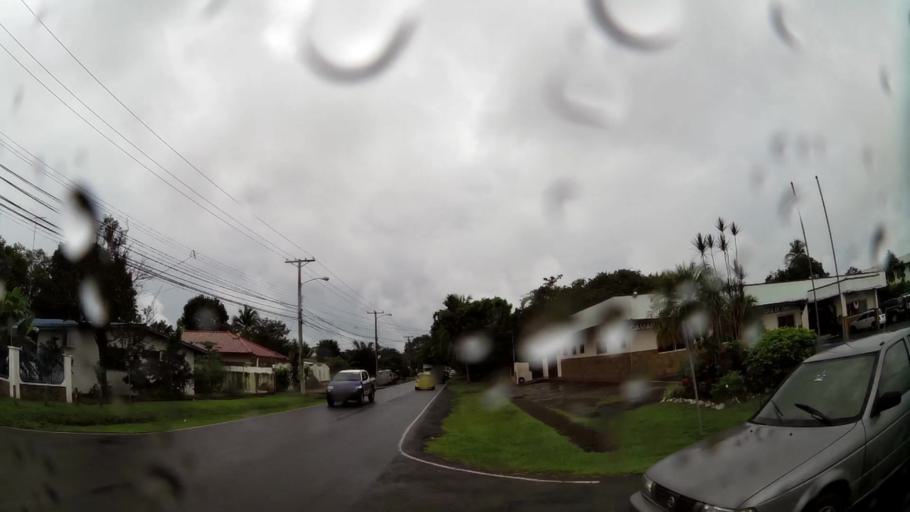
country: PA
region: Chiriqui
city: David
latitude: 8.4320
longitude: -82.4357
